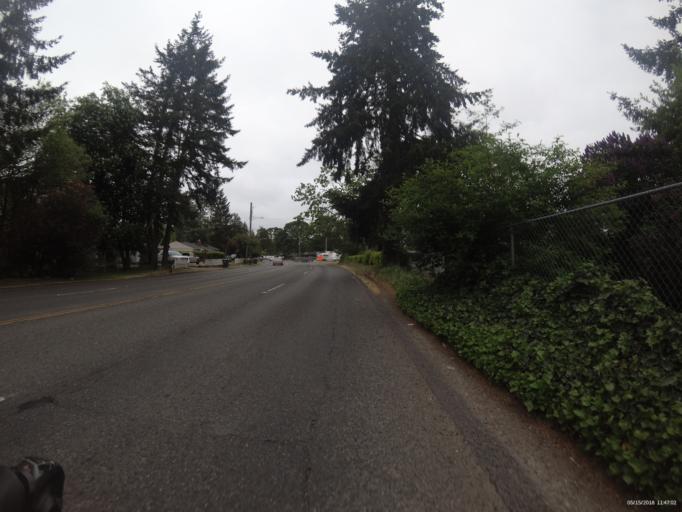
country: US
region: Washington
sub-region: Pierce County
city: Lakewood
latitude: 47.1800
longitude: -122.5272
